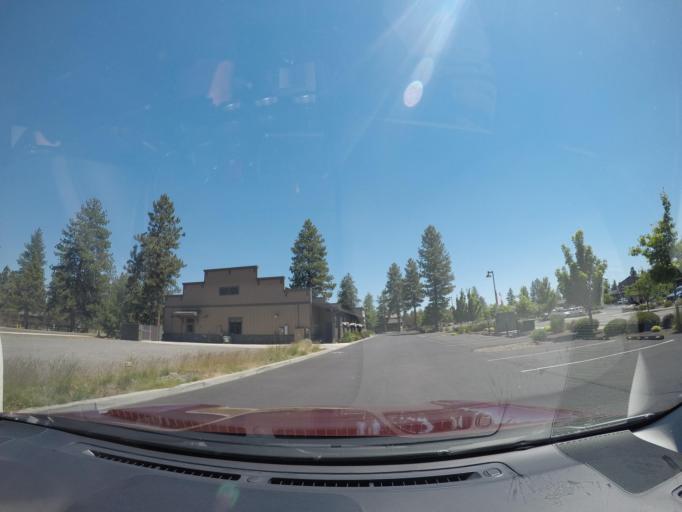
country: US
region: Oregon
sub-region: Deschutes County
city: Sisters
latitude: 44.2971
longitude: -121.5615
